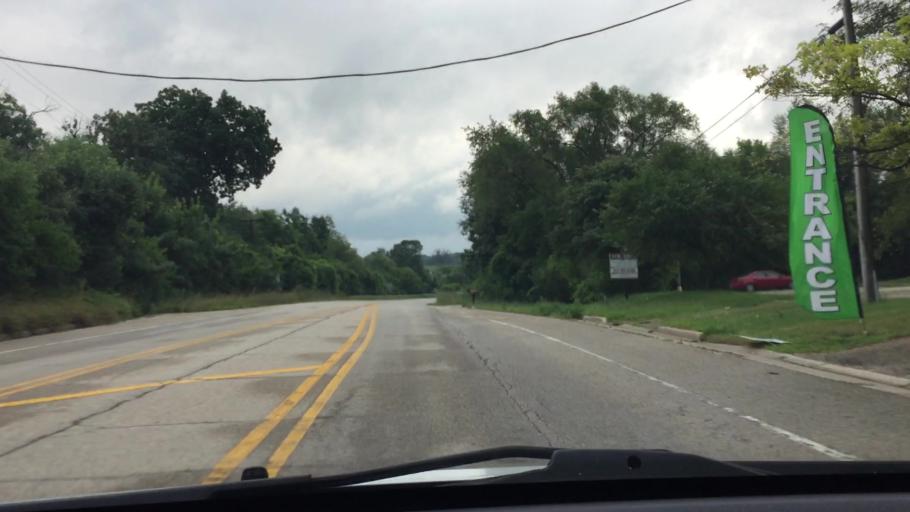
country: US
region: Illinois
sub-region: McHenry County
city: Hebron
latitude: 42.4773
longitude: -88.4363
